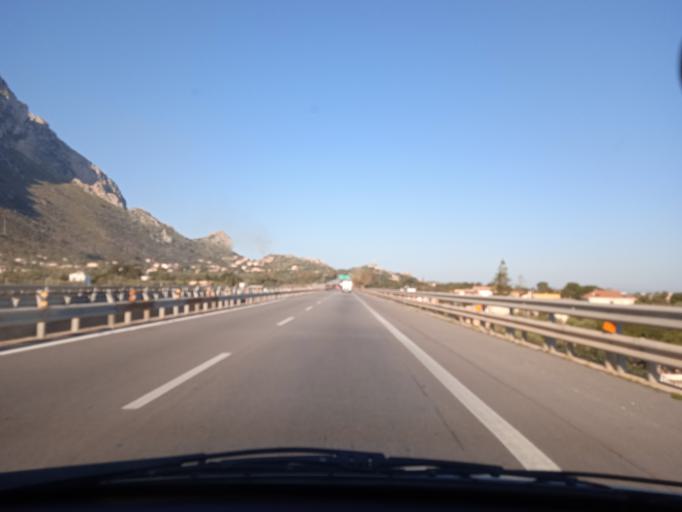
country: IT
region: Sicily
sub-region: Palermo
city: Carini
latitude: 38.1799
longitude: 13.1441
